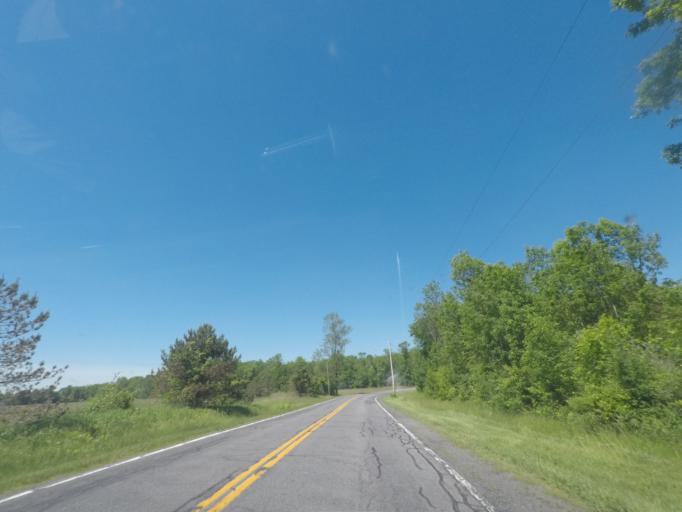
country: US
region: New York
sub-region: Saratoga County
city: Country Knolls
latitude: 42.8594
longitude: -73.8389
